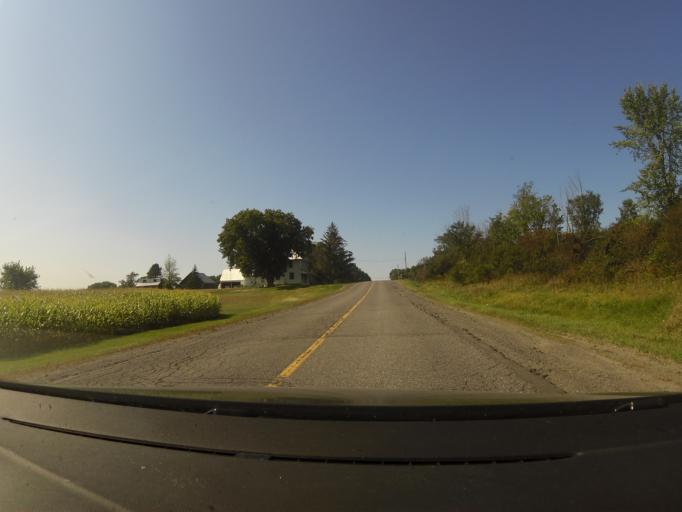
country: CA
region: Ontario
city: Arnprior
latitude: 45.3772
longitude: -76.1229
